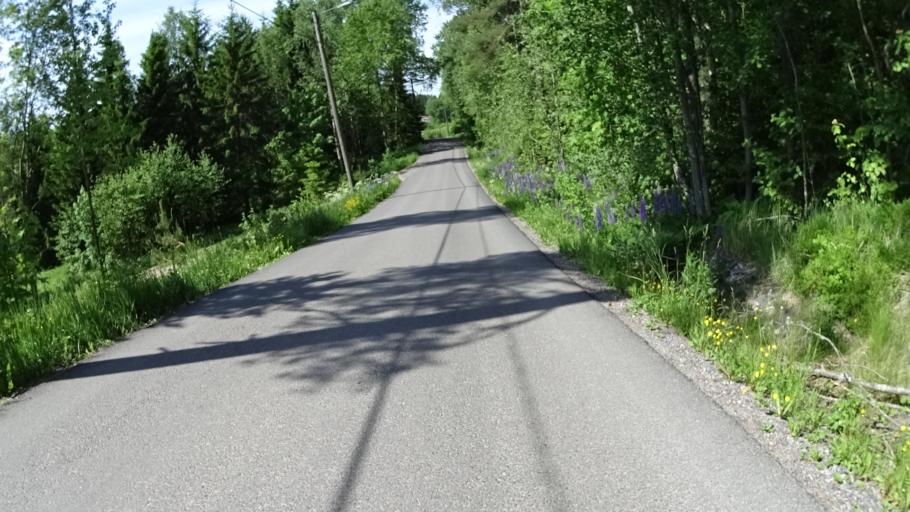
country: FI
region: Uusimaa
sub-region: Helsinki
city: Kauniainen
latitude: 60.3183
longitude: 24.7233
